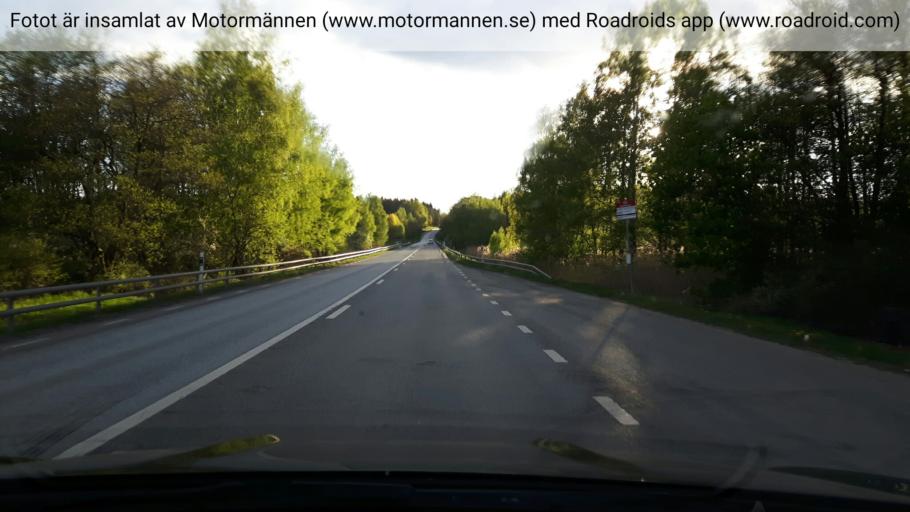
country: SE
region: Stockholm
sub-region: Vaxholms Kommun
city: Resaro
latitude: 59.4227
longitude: 18.2935
